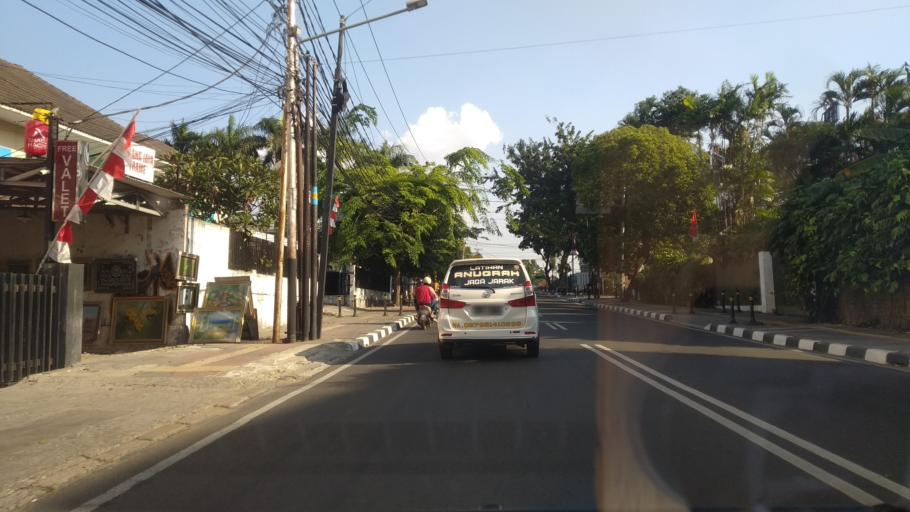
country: ID
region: Banten
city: South Tangerang
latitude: -6.2588
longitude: 106.7679
